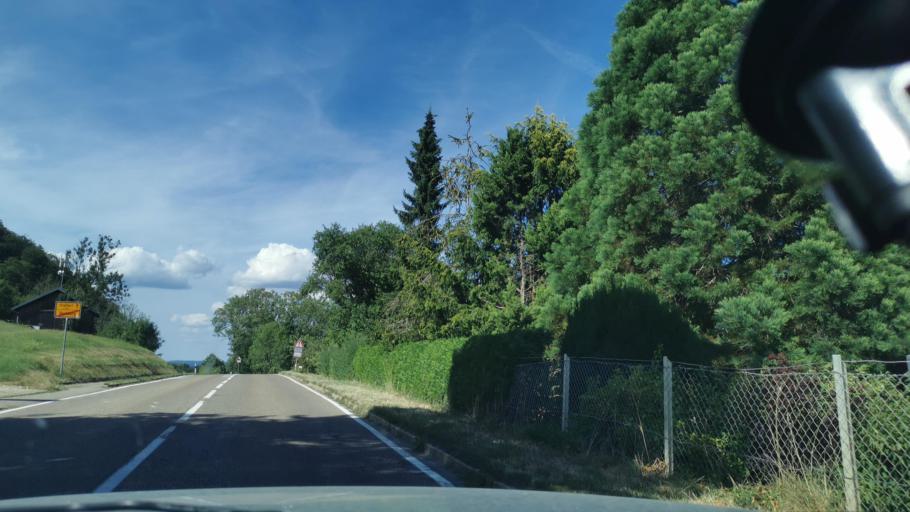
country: DE
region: Baden-Wuerttemberg
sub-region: Regierungsbezirk Stuttgart
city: Waldstetten
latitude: 48.7534
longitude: 9.7944
